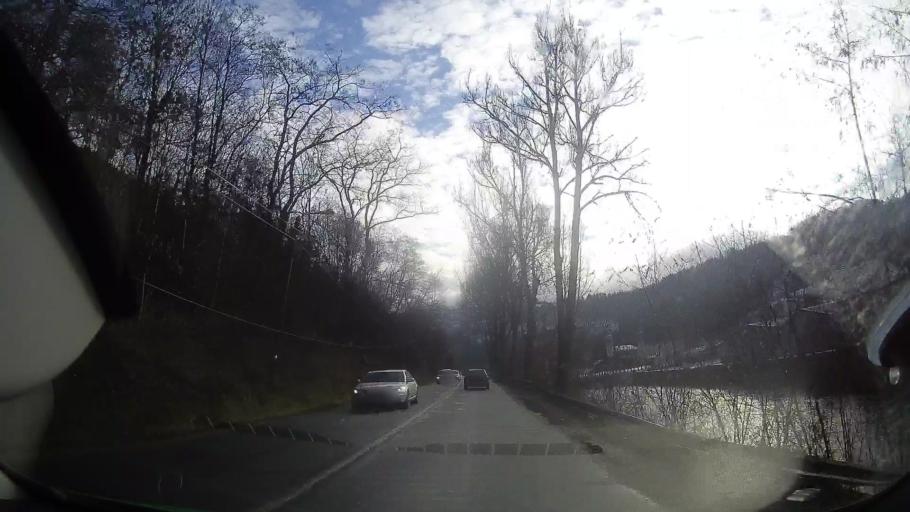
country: RO
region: Alba
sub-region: Oras Campeni
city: Campeni
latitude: 46.3620
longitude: 23.0606
